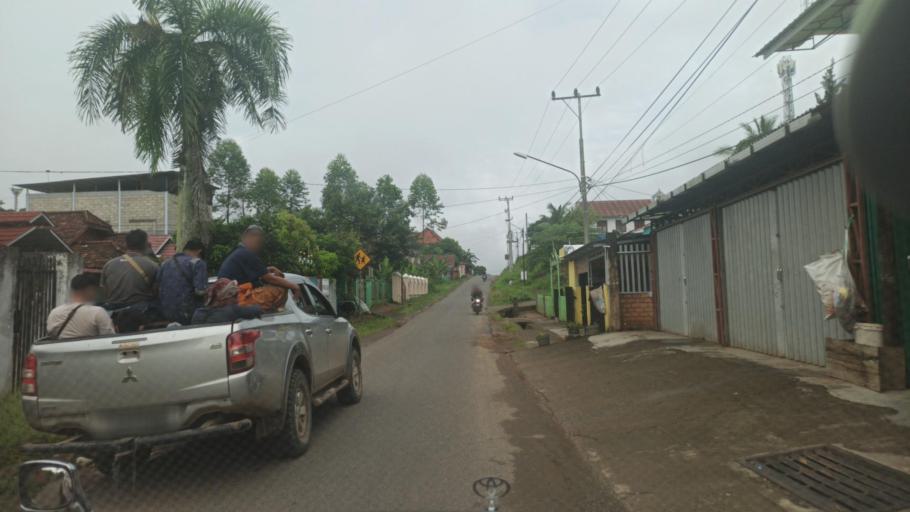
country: ID
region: South Sumatra
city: Gunungmegang Dalam
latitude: -3.2669
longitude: 103.8131
